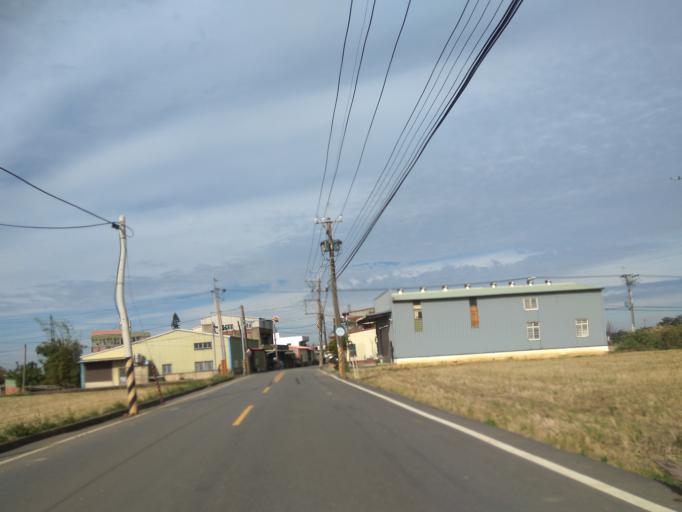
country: TW
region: Taiwan
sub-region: Hsinchu
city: Zhubei
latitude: 24.9532
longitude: 121.1280
